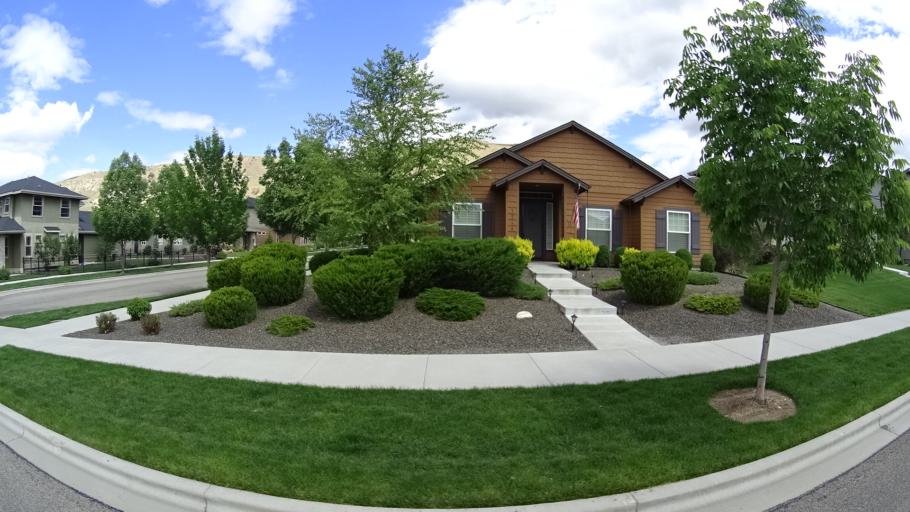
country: US
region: Idaho
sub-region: Ada County
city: Boise
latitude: 43.5780
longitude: -116.1350
